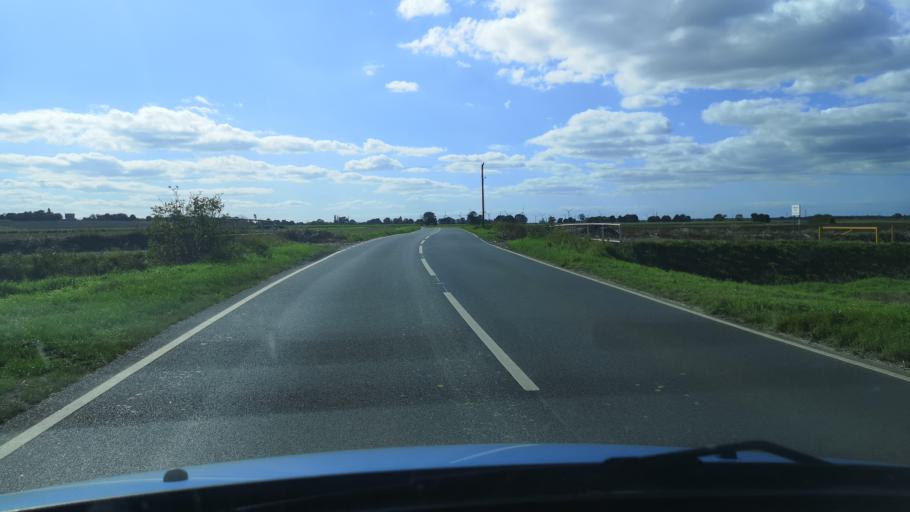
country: GB
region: England
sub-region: North Lincolnshire
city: Crowle
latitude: 53.6185
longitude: -0.8134
